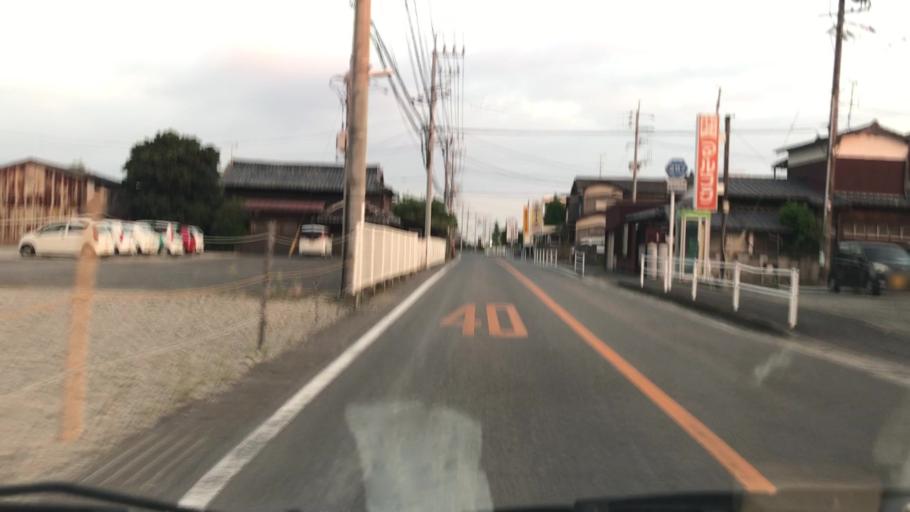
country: JP
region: Saga Prefecture
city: Saga-shi
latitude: 33.2426
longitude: 130.2580
